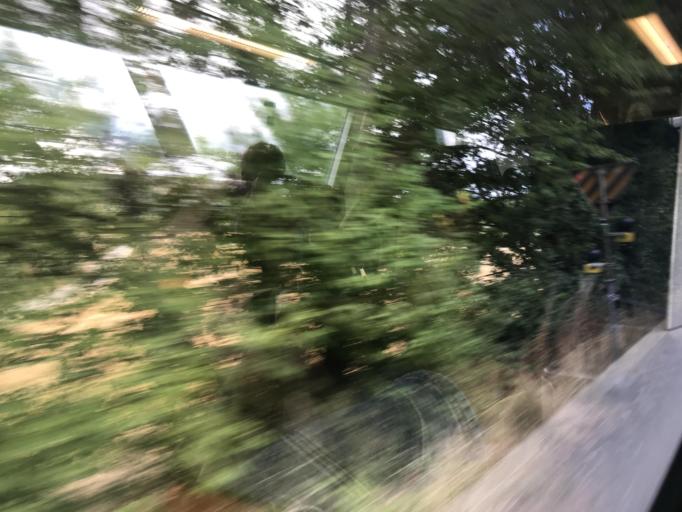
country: DE
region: Bavaria
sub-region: Regierungsbezirk Unterfranken
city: Elfershausen
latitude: 50.1292
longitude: 9.9461
